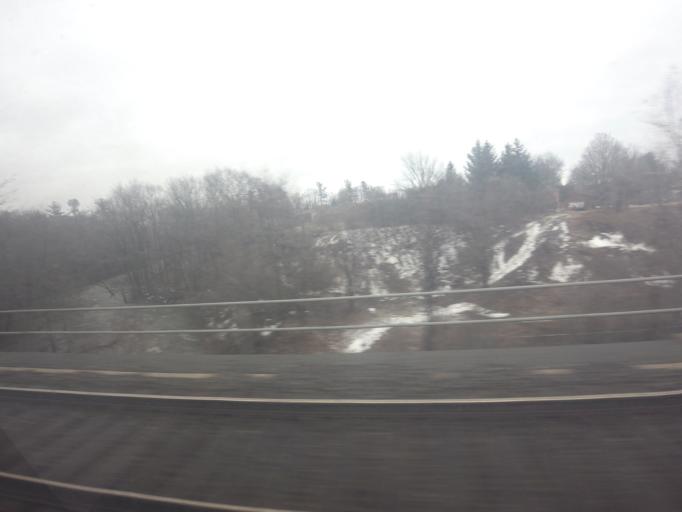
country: CA
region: Ontario
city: Kingston
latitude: 44.2396
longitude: -76.6215
